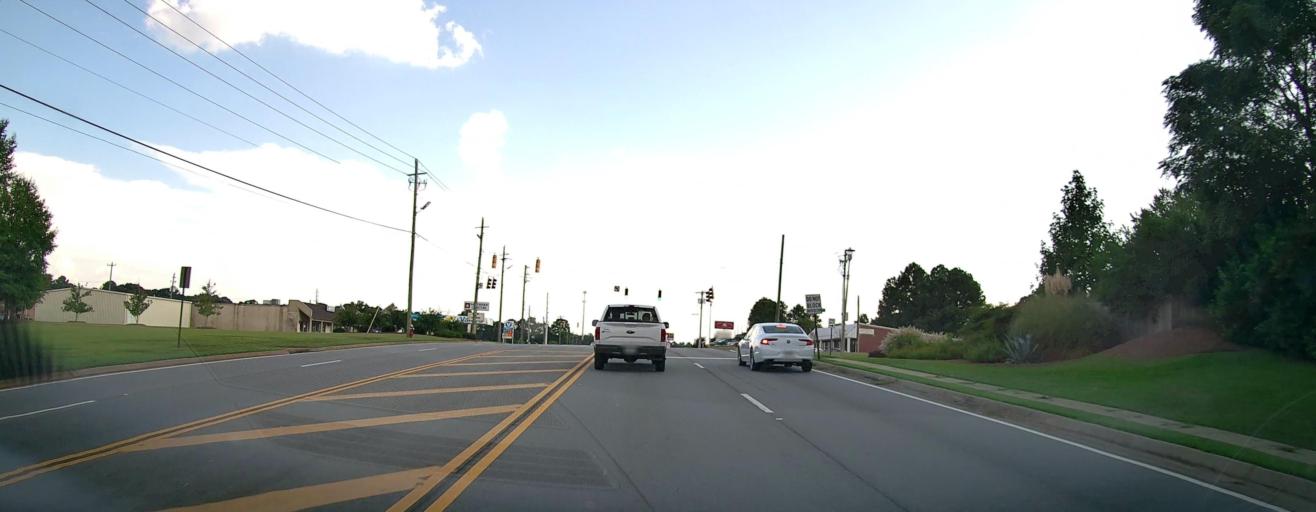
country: US
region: Georgia
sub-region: Houston County
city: Warner Robins
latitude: 32.5797
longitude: -83.6241
